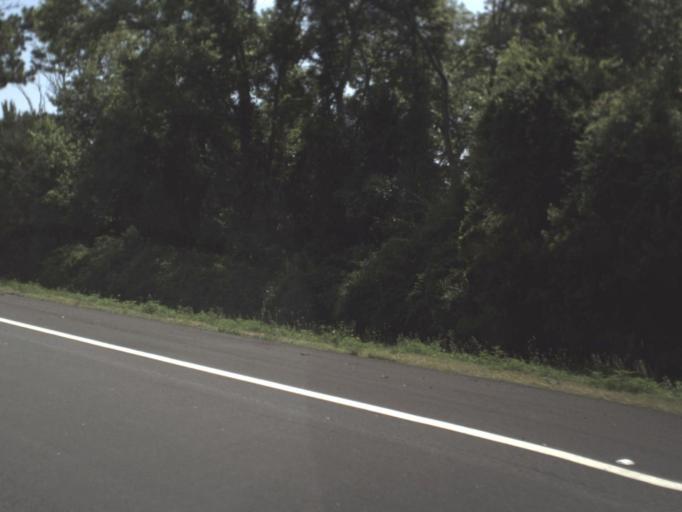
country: US
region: Georgia
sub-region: Camden County
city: Kingsland
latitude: 30.7313
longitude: -81.6609
